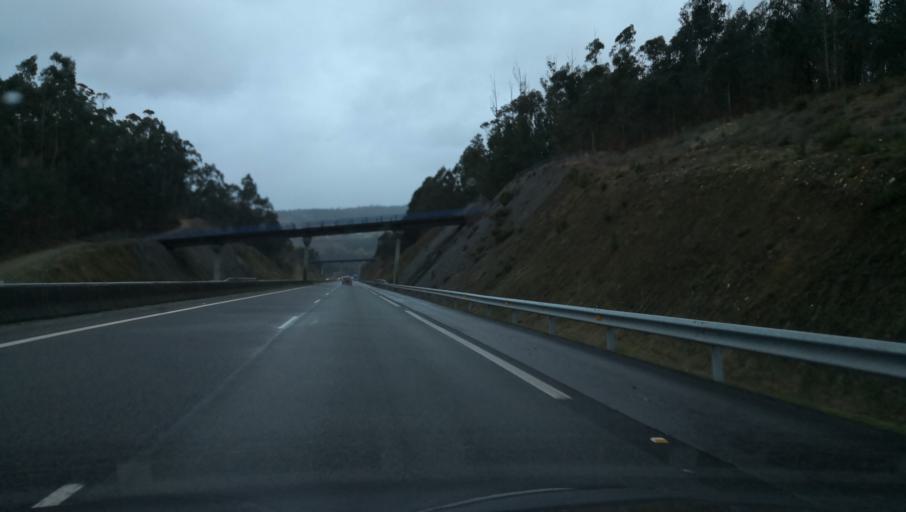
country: ES
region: Galicia
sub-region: Provincia da Coruna
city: Vedra
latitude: 42.8237
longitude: -8.5064
